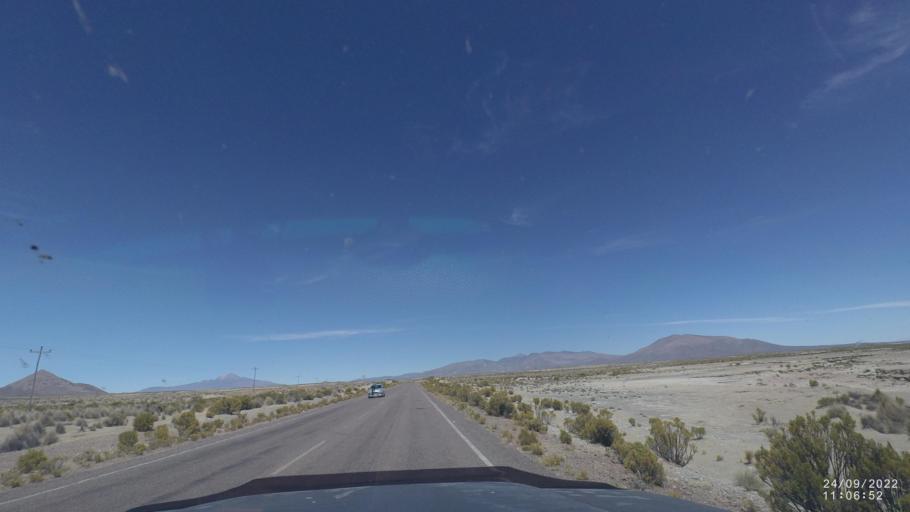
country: BO
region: Oruro
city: Challapata
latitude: -19.4787
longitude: -67.4339
